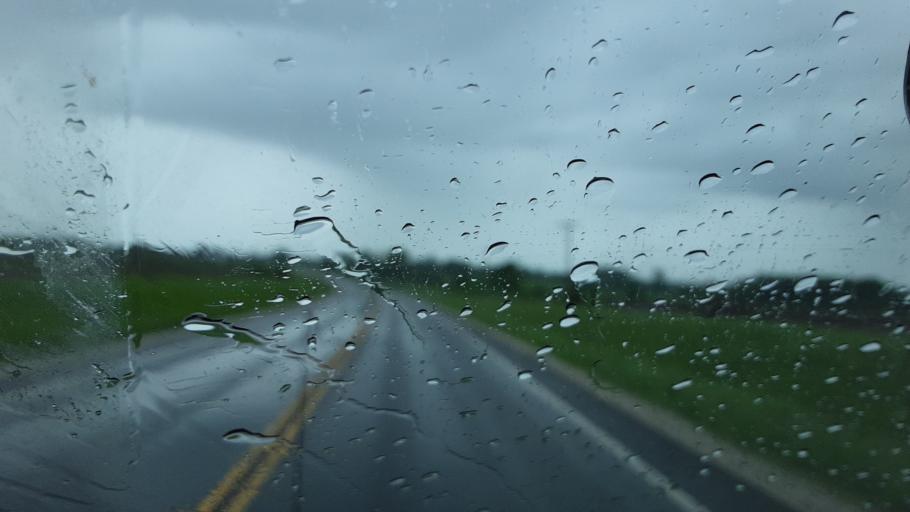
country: US
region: Missouri
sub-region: Monroe County
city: Paris
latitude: 39.4800
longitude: -92.1733
